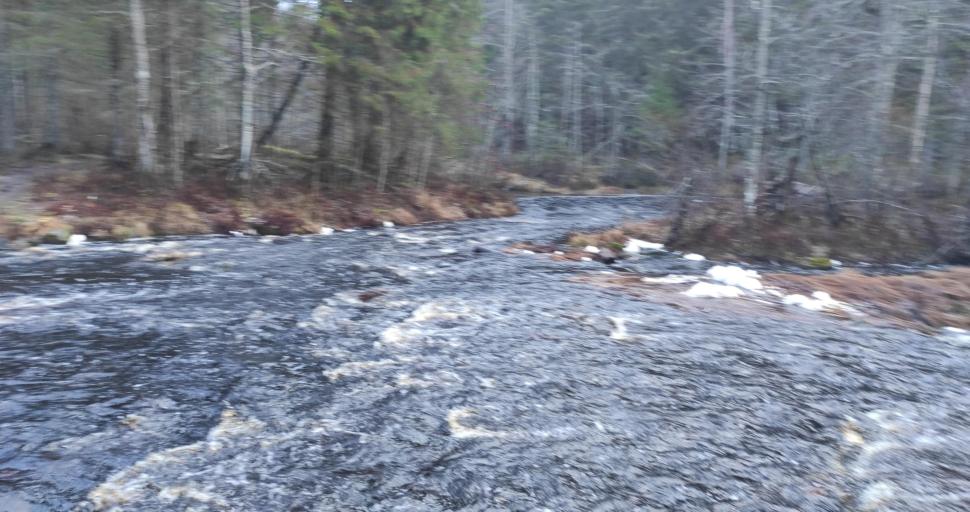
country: RU
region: Republic of Karelia
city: Pitkyaranta
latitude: 61.7531
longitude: 31.4106
